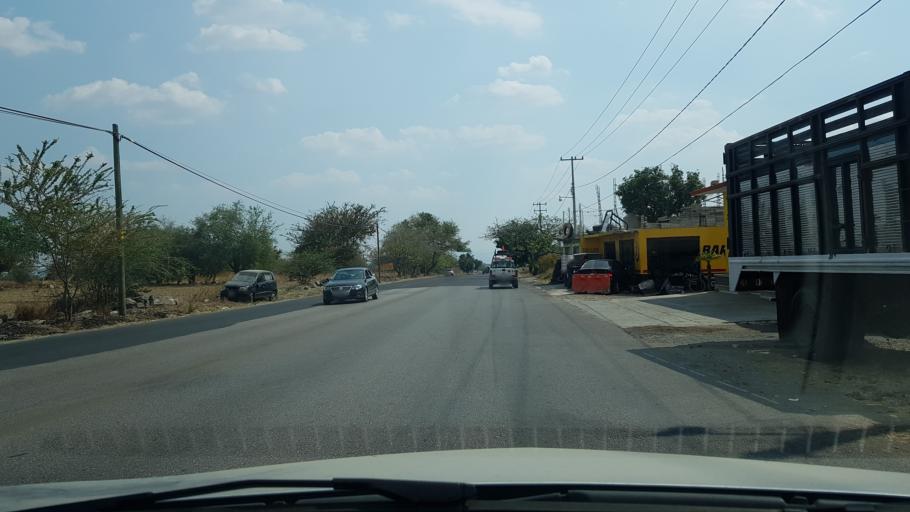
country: MX
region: Morelos
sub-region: Temoac
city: Huazulco
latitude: 18.7460
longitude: -98.7835
